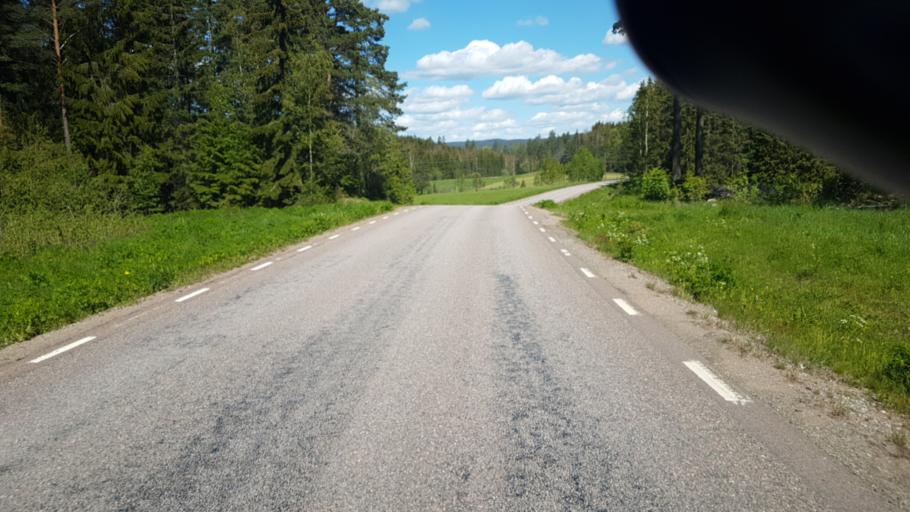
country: SE
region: Vaermland
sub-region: Arvika Kommun
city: Arvika
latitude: 59.6241
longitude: 12.7959
